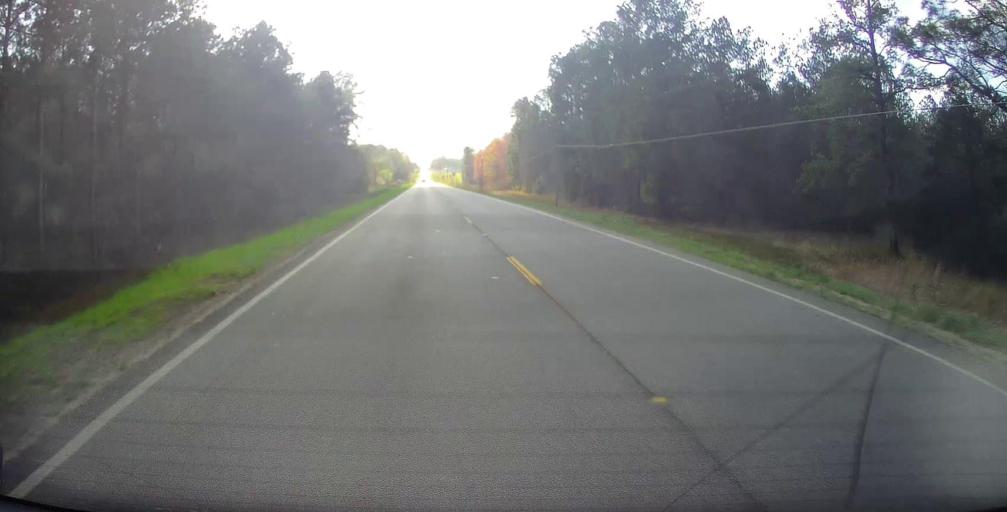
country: US
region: Georgia
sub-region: Wheeler County
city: Alamo
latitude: 32.1548
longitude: -82.7574
